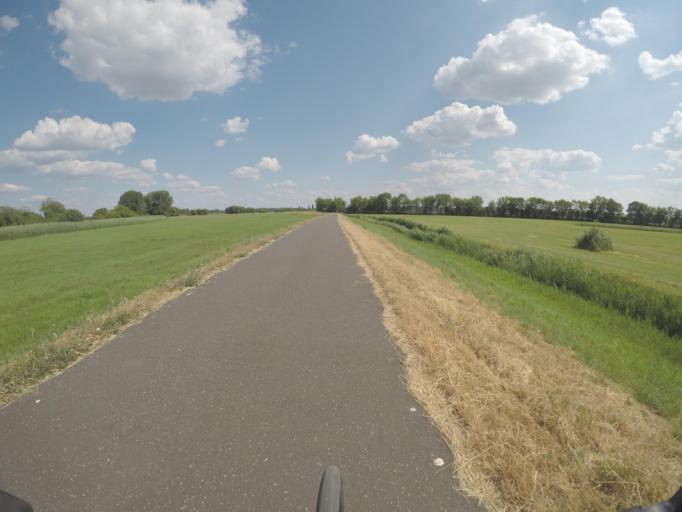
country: DE
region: Brandenburg
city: Ketzin
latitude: 52.4563
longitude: 12.8681
